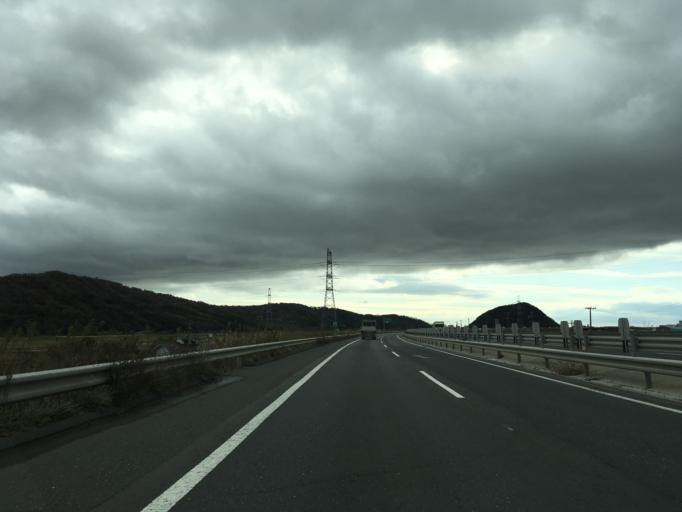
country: JP
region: Miyagi
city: Ishinomaki
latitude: 38.4831
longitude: 141.2925
